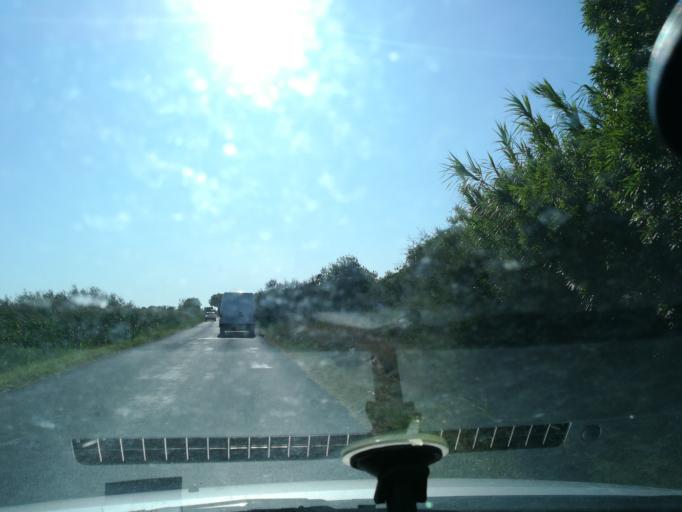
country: FR
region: Languedoc-Roussillon
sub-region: Departement de l'Herault
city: Vias
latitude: 43.2946
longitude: 3.3957
